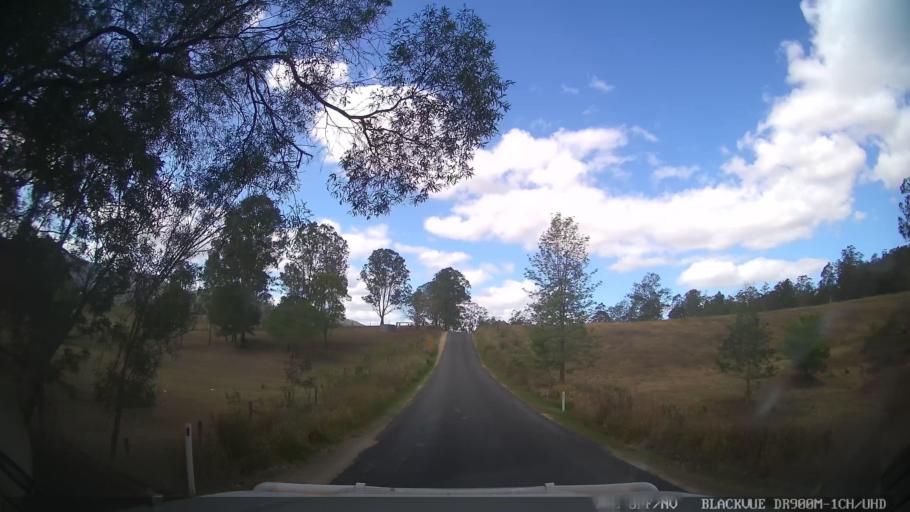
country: AU
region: Queensland
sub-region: Sunshine Coast
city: Nambour
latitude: -26.6300
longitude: 152.6755
